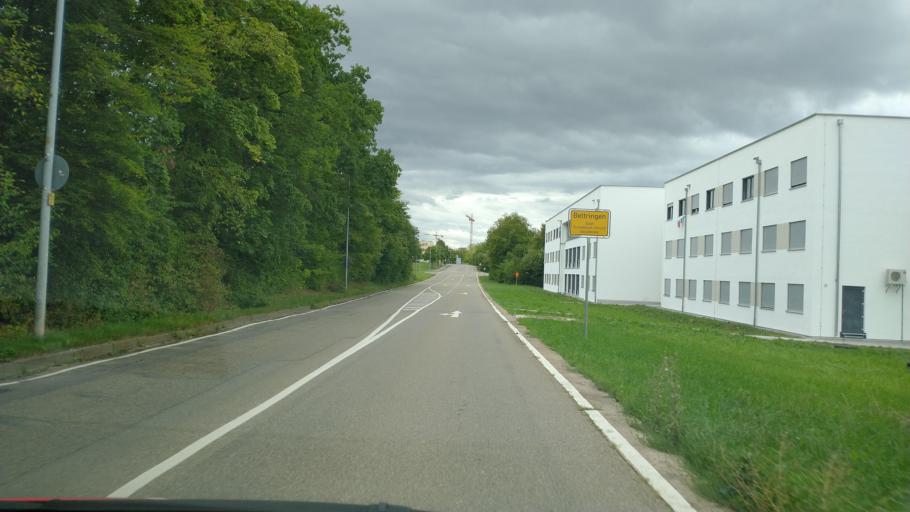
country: DE
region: Baden-Wuerttemberg
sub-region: Regierungsbezirk Stuttgart
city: Waldstetten
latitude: 48.7941
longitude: 9.8346
